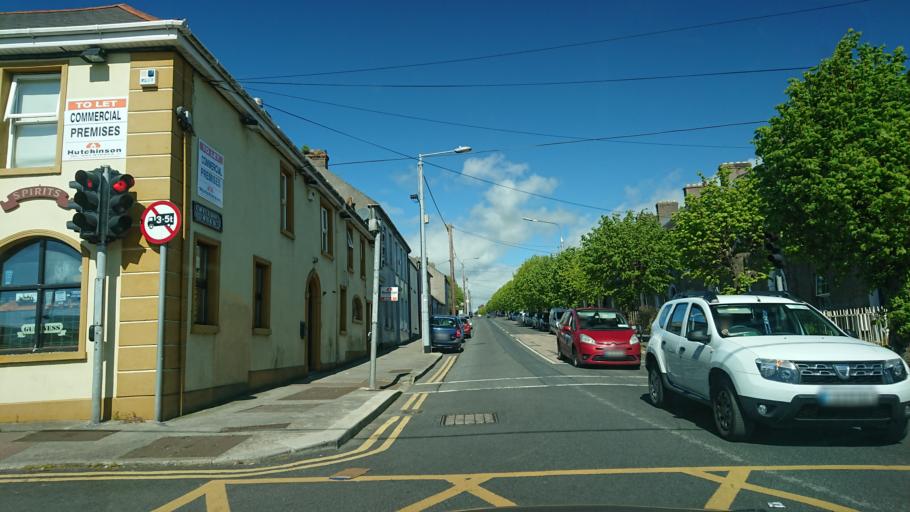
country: IE
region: Munster
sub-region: Waterford
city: Waterford
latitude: 52.2615
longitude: -7.1224
